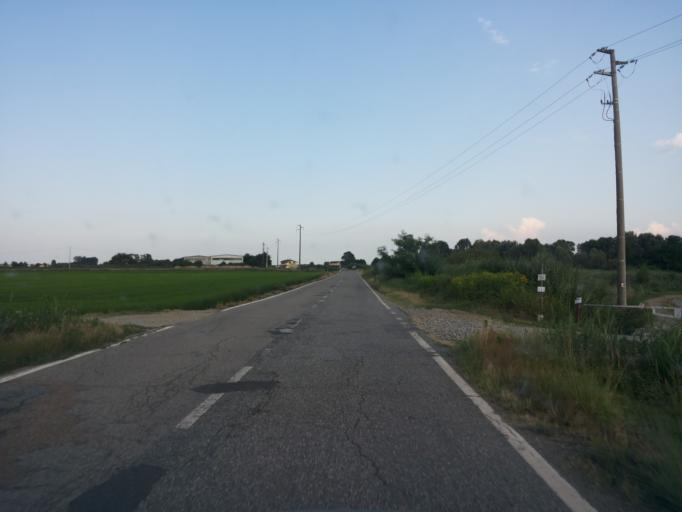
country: IT
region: Piedmont
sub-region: Provincia di Vercelli
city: Pezzana
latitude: 45.2603
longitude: 8.4577
